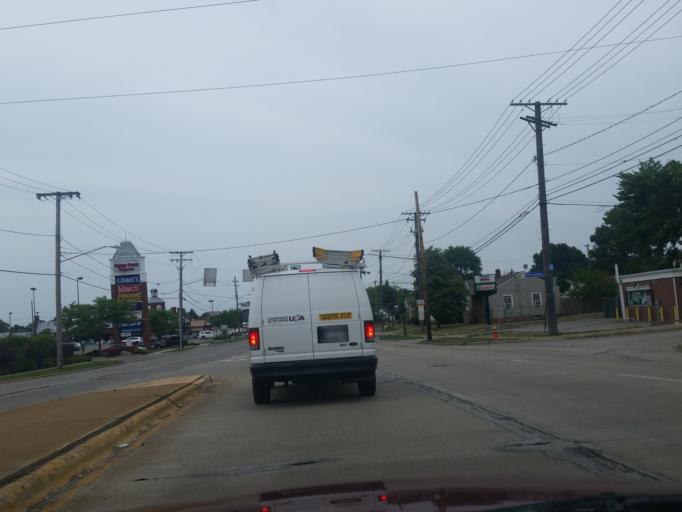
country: US
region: Ohio
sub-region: Cuyahoga County
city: Brooklyn
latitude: 41.4233
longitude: -81.7343
